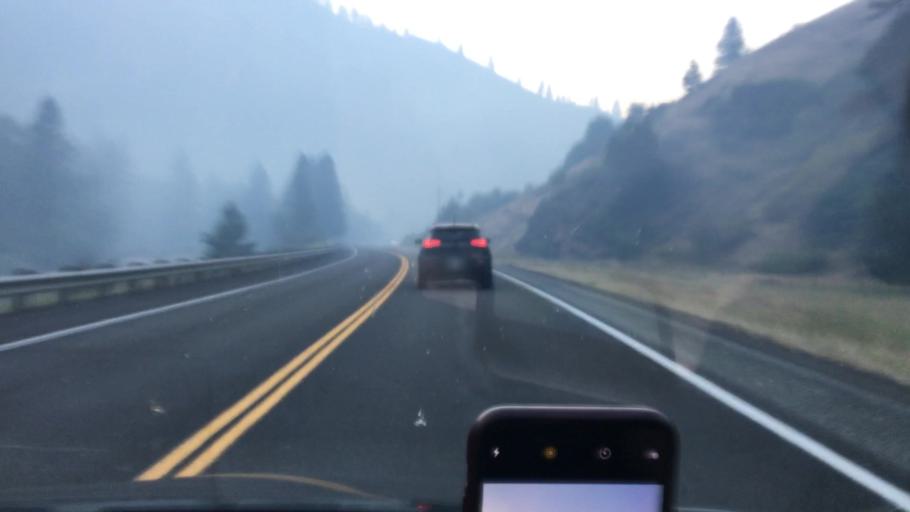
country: US
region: Idaho
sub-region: Valley County
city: McCall
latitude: 45.2682
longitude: -116.3426
